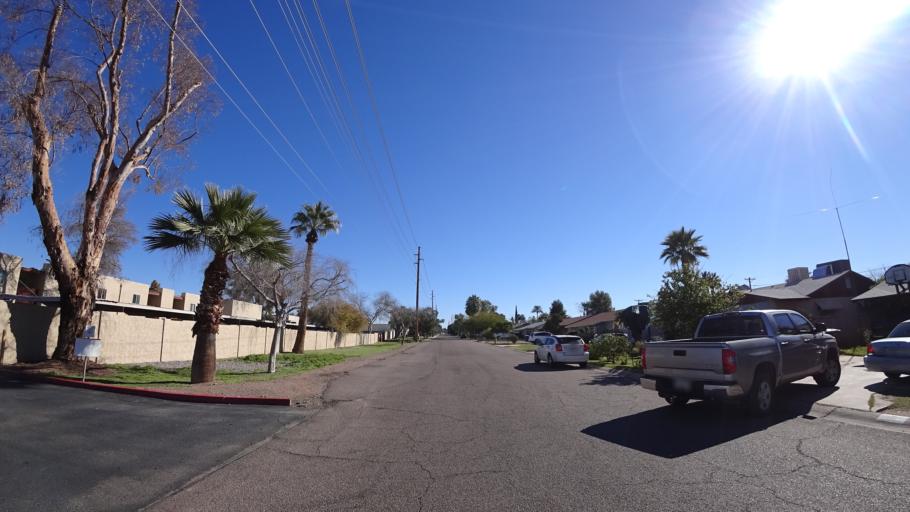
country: US
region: Arizona
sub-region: Maricopa County
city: Paradise Valley
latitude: 33.4783
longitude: -111.9684
